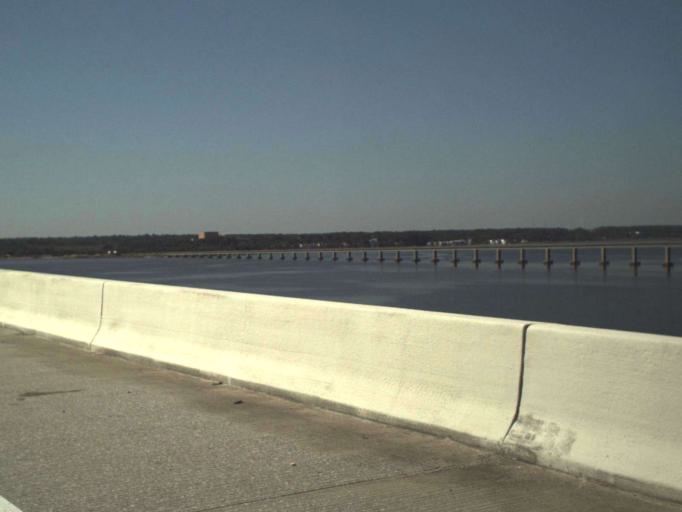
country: US
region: Florida
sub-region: Escambia County
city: Ferry Pass
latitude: 30.5182
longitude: -87.1457
